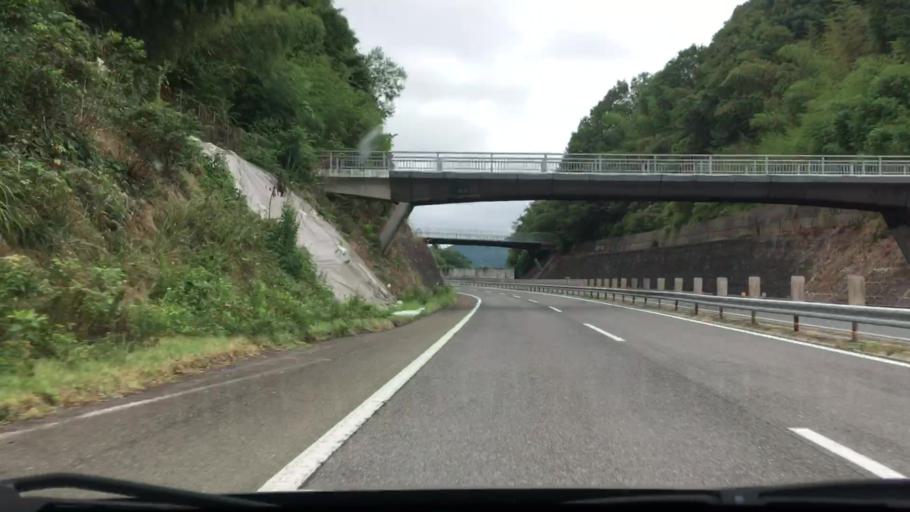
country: JP
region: Hiroshima
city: Shobara
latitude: 34.8394
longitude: 132.9878
